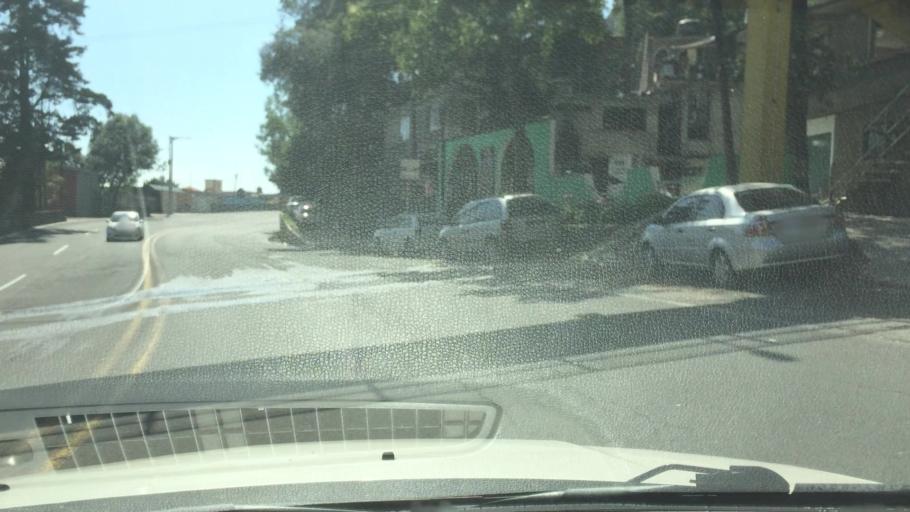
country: MX
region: Mexico City
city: Tlalpan
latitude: 19.2505
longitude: -99.1761
